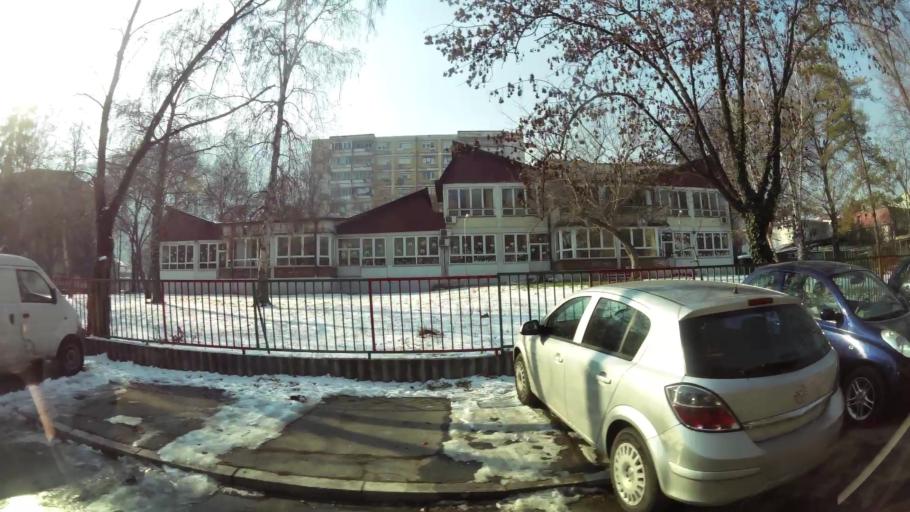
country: MK
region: Kisela Voda
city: Usje
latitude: 41.9735
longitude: 21.4414
